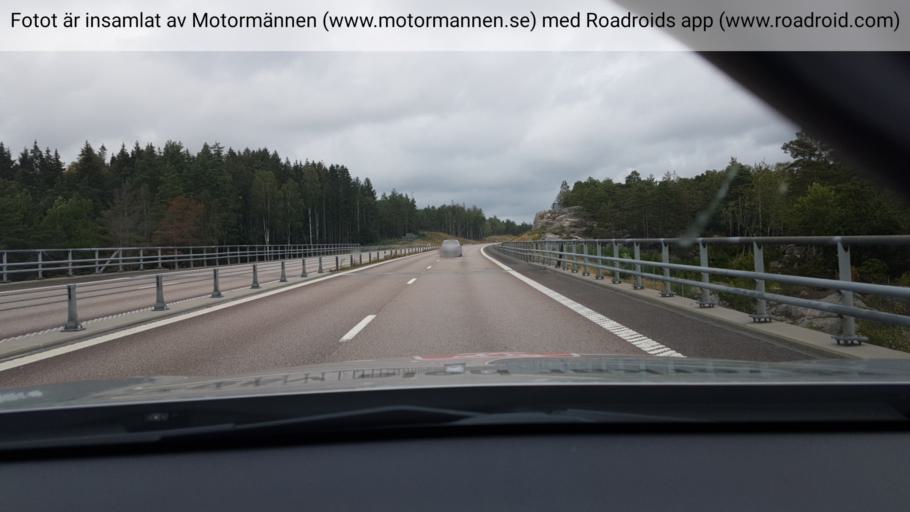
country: SE
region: Vaestra Goetaland
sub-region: Tanums Kommun
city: Tanumshede
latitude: 58.7773
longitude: 11.2735
